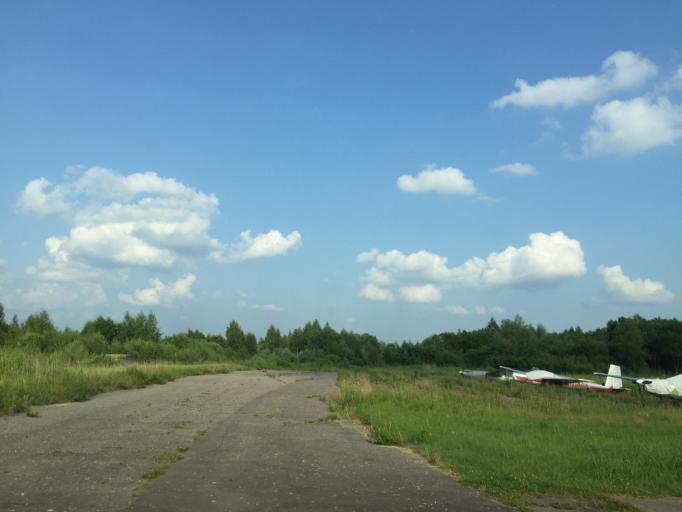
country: LV
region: Jelgava
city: Jelgava
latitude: 56.6706
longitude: 23.6894
